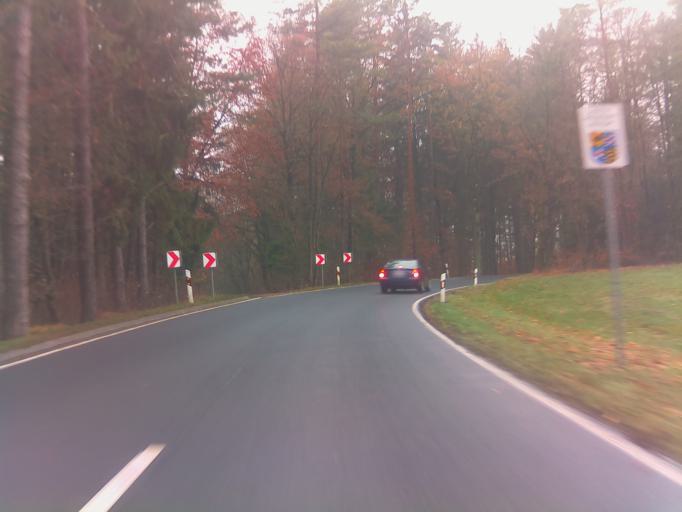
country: DE
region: Thuringia
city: Leutersdorf
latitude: 50.4803
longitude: 10.5613
